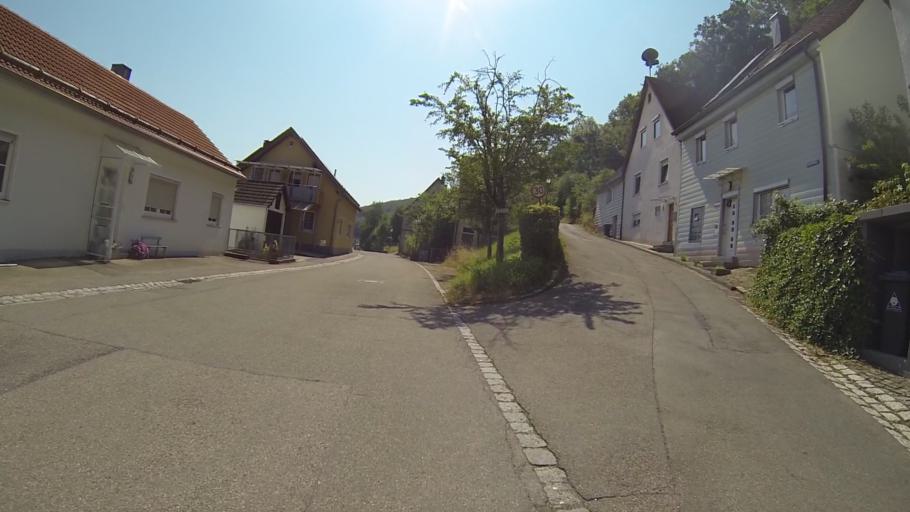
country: DE
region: Baden-Wuerttemberg
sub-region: Regierungsbezirk Stuttgart
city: Konigsbronn
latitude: 48.7361
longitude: 10.1152
